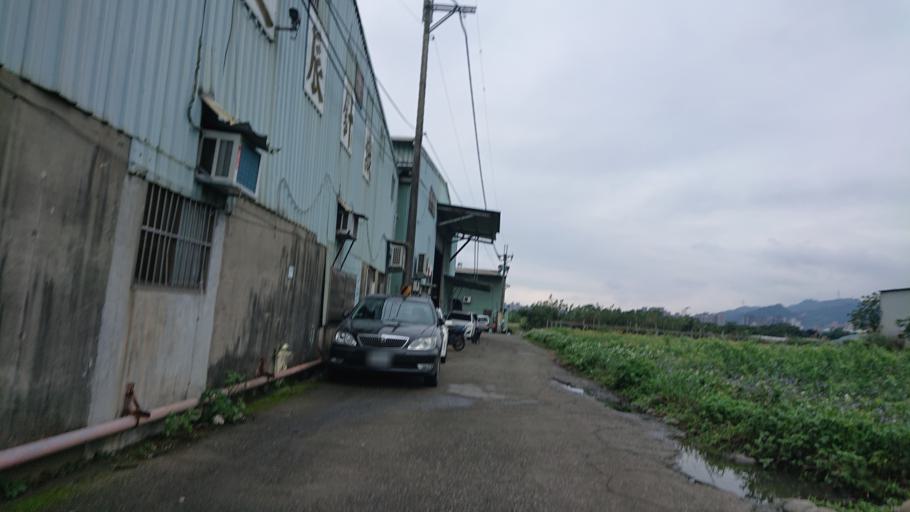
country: TW
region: Taiwan
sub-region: Taoyuan
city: Taoyuan
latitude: 24.9419
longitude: 121.3914
